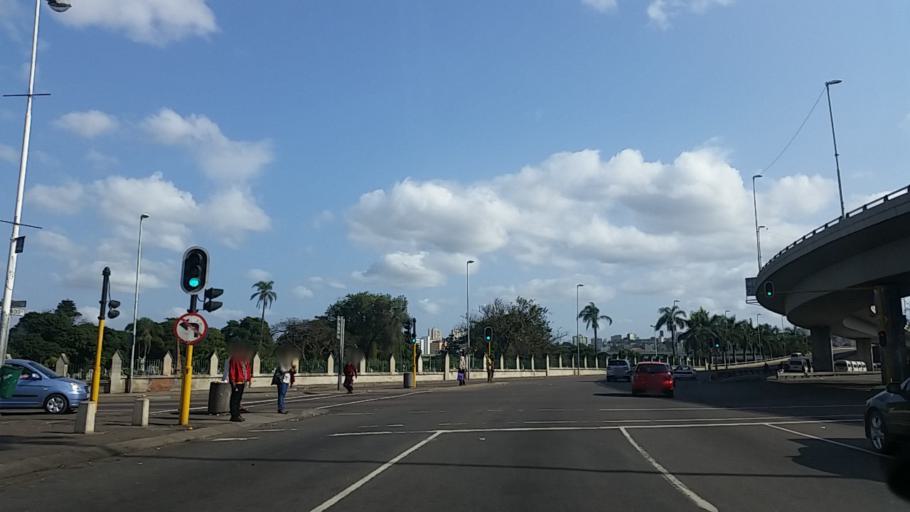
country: ZA
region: KwaZulu-Natal
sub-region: eThekwini Metropolitan Municipality
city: Durban
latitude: -29.8584
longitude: 31.0160
